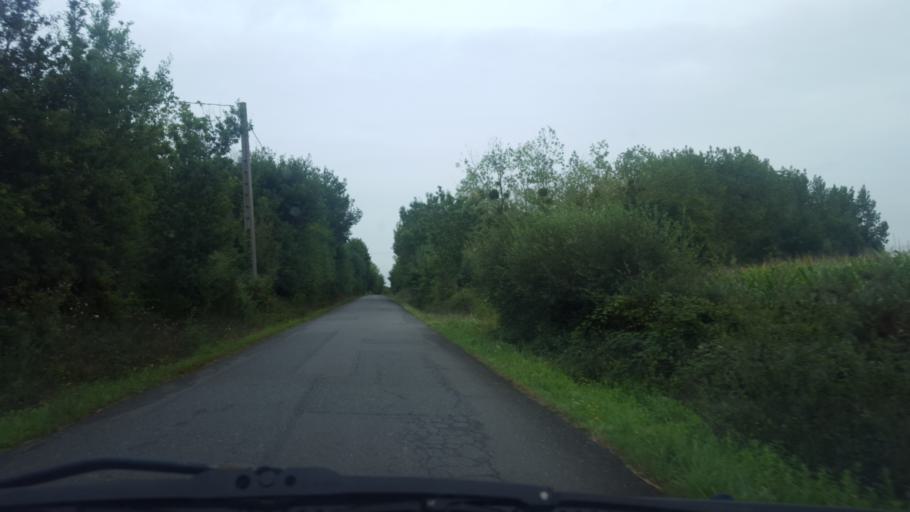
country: FR
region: Pays de la Loire
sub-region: Departement de la Loire-Atlantique
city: Saint-Philbert-de-Grand-Lieu
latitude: 47.0413
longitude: -1.6630
